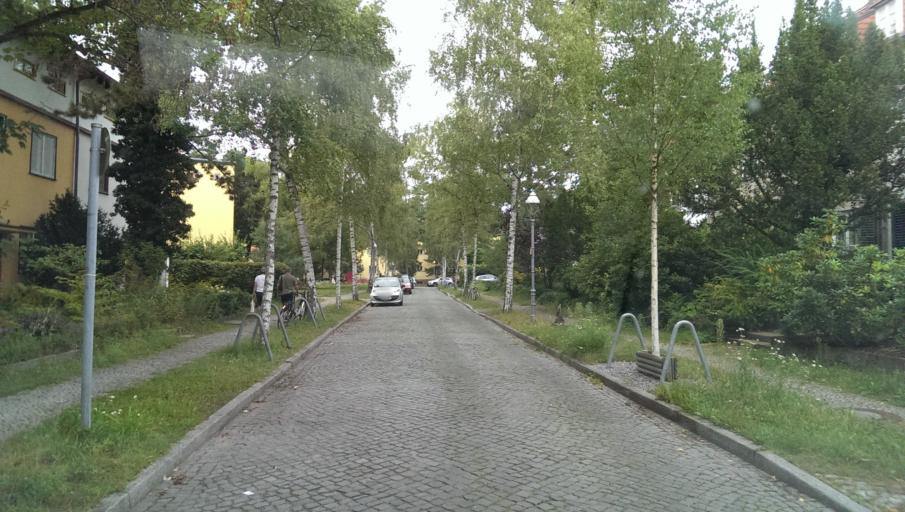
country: DE
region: Berlin
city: Zehlendorf Bezirk
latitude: 52.4495
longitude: 13.2601
